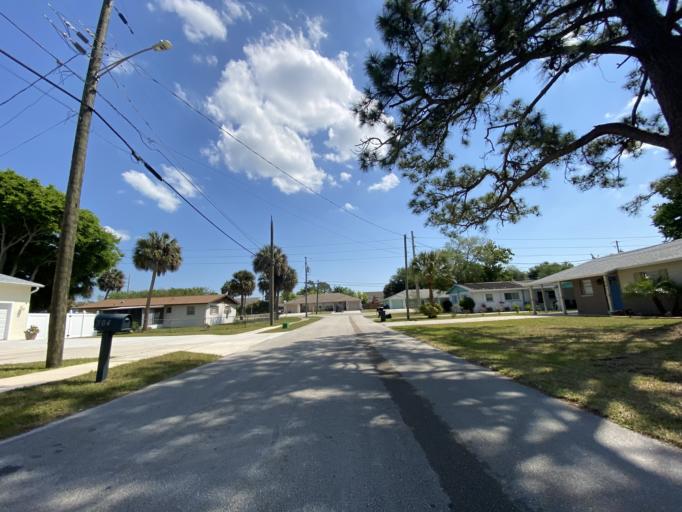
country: US
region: Florida
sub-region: Volusia County
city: South Daytona
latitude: 29.1714
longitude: -81.0075
